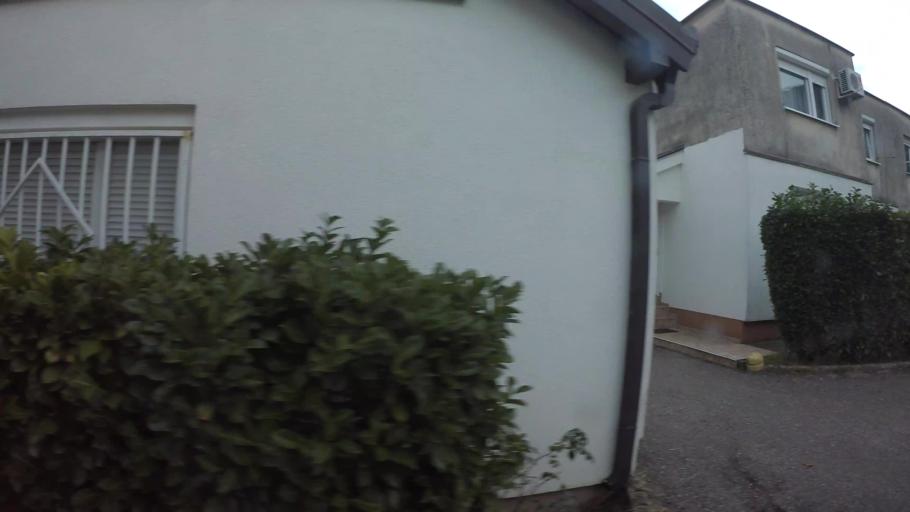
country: BA
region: Federation of Bosnia and Herzegovina
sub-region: Hercegovacko-Bosanski Kanton
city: Mostar
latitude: 43.3351
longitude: 17.7981
